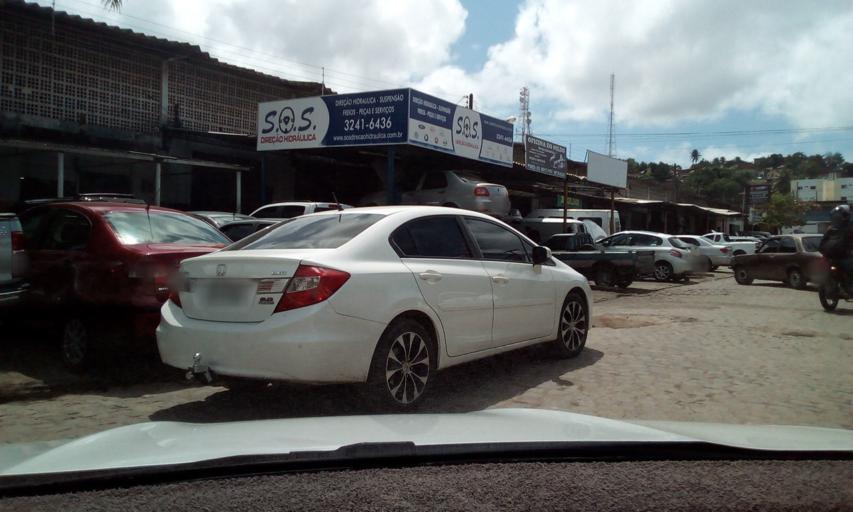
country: BR
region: Paraiba
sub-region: Joao Pessoa
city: Joao Pessoa
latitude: -7.1293
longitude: -34.8889
